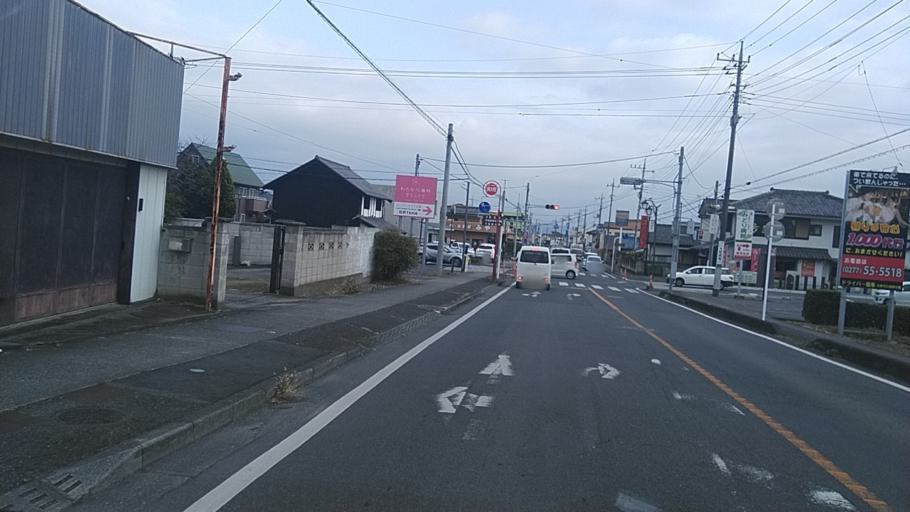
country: JP
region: Gunma
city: Omamacho-omama
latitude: 36.4154
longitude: 139.2979
